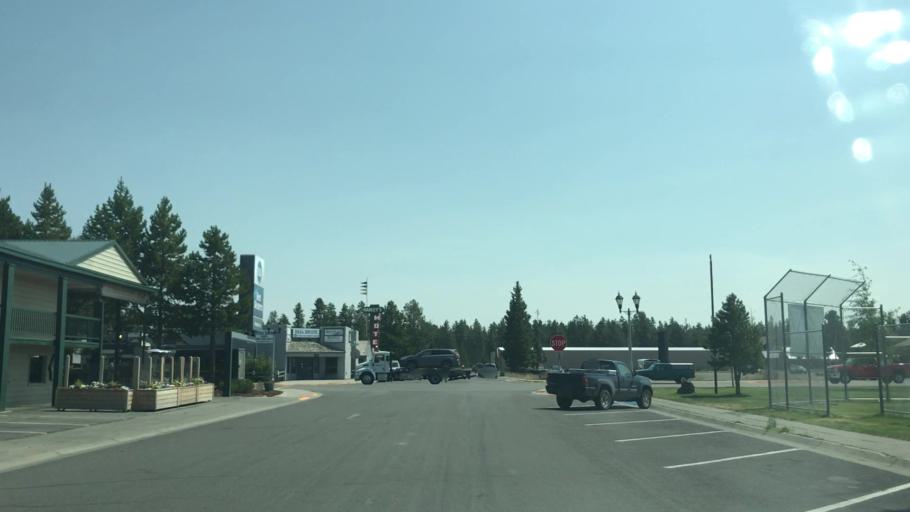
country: US
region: Montana
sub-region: Gallatin County
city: West Yellowstone
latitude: 44.6639
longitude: -111.1005
